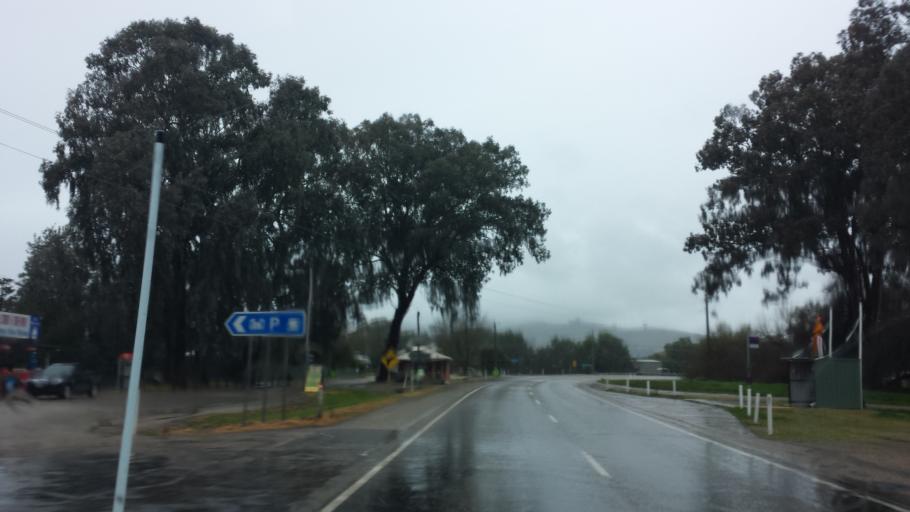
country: AU
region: Victoria
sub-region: Wangaratta
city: Wangaratta
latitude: -36.4329
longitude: 146.5405
